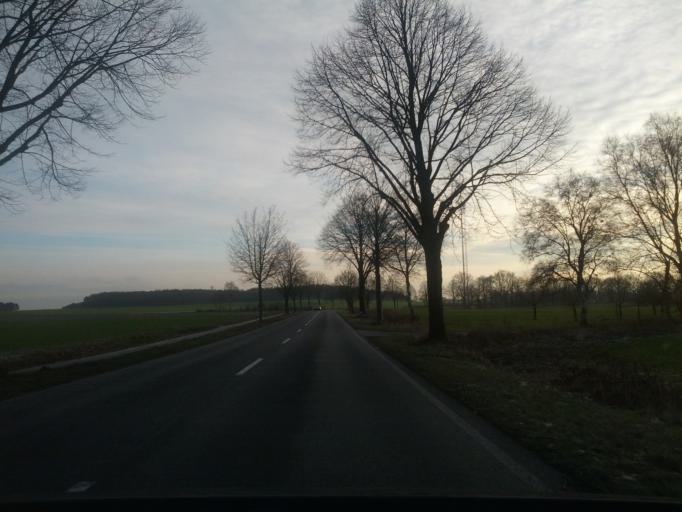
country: DE
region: Lower Saxony
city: Beckdorf
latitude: 53.3995
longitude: 9.6102
